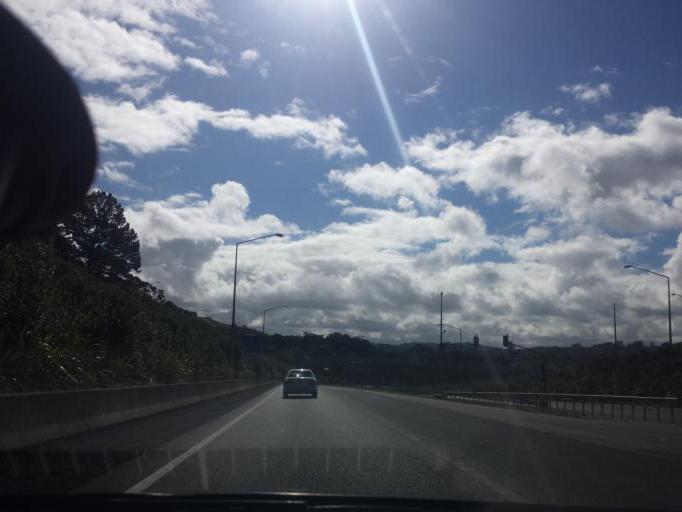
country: NZ
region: Auckland
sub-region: Auckland
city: Warkworth
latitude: -36.5332
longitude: 174.6790
